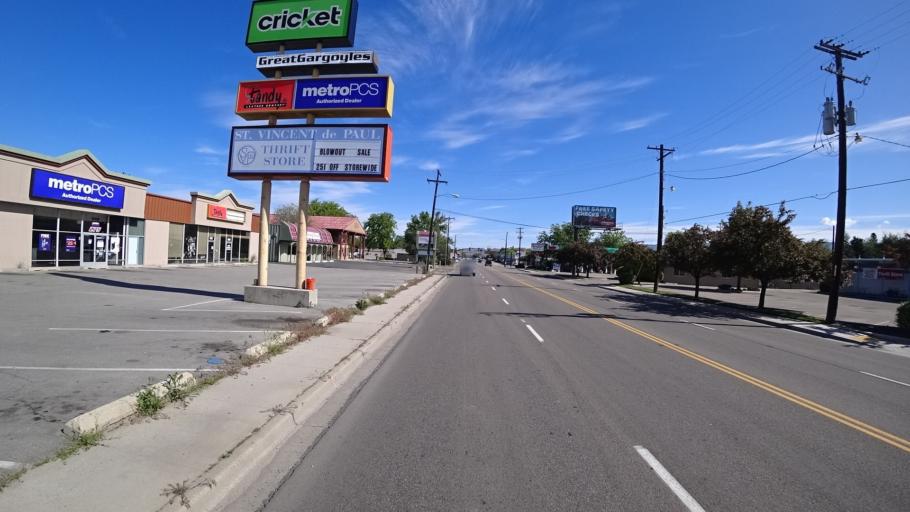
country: US
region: Idaho
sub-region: Ada County
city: Garden City
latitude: 43.6067
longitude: -116.2435
